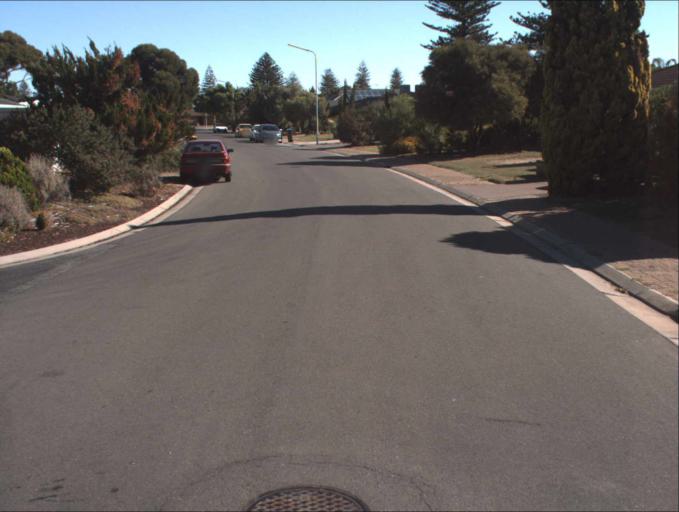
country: AU
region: South Australia
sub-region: Port Adelaide Enfield
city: Birkenhead
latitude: -34.7793
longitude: 138.4909
